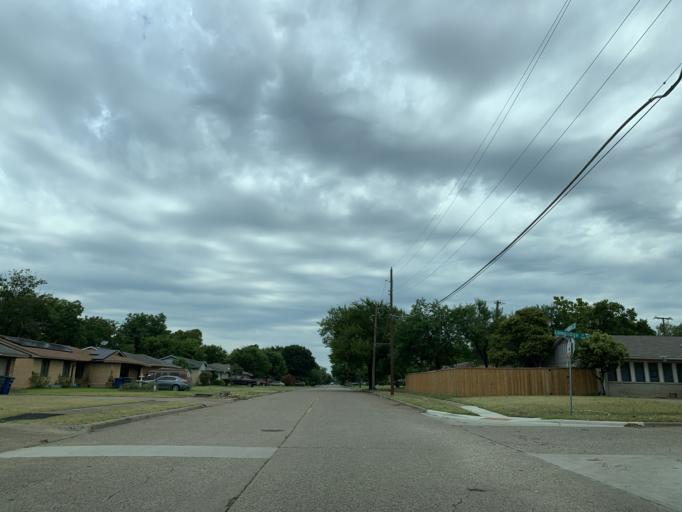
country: US
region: Texas
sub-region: Dallas County
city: DeSoto
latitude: 32.6590
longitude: -96.8309
